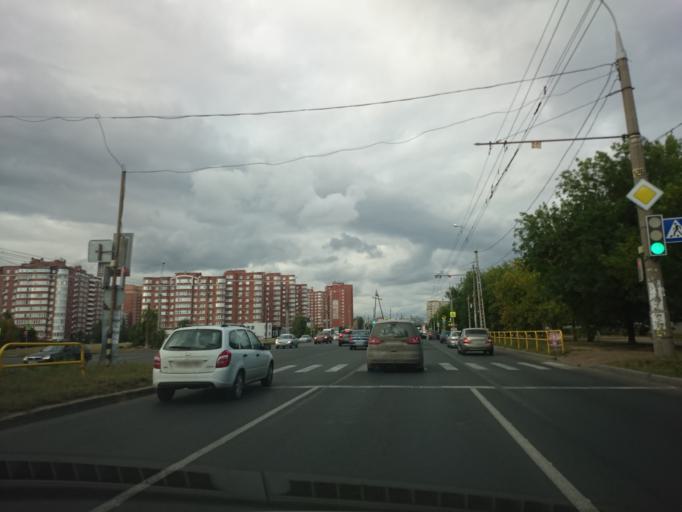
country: RU
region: Samara
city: Tol'yatti
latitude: 53.5119
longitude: 49.3056
